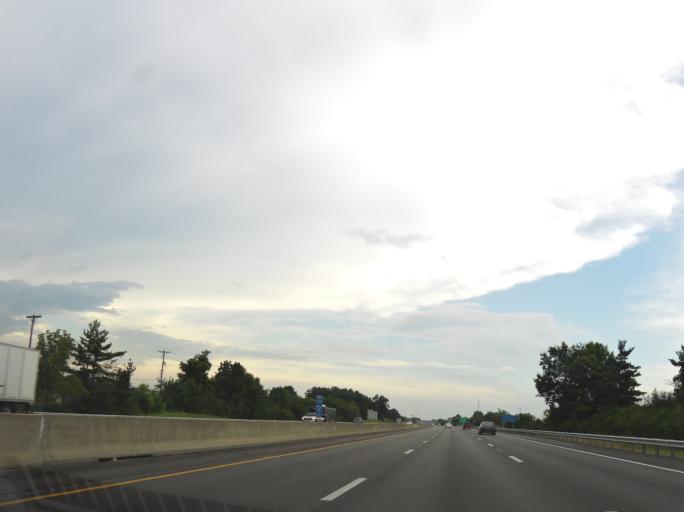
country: US
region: Kentucky
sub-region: Madison County
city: Richmond
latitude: 37.7506
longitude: -84.3204
